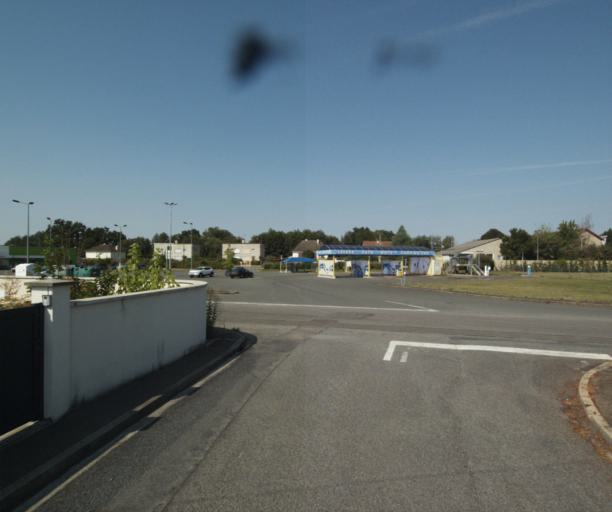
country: FR
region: Bourgogne
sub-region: Departement de Saone-et-Loire
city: Gueugnon
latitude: 46.5982
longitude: 4.0527
